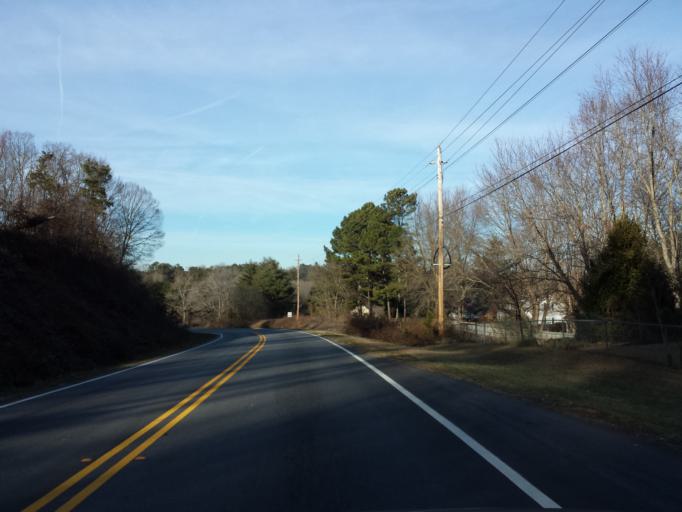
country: US
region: Georgia
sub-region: Cobb County
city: Kennesaw
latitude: 34.0213
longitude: -84.5479
